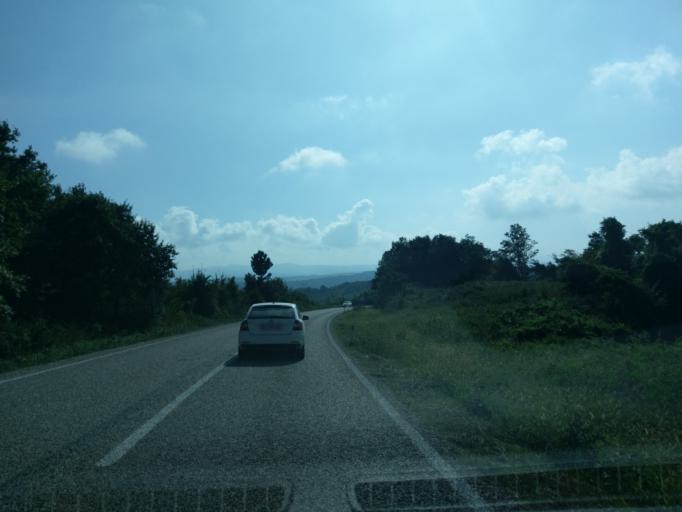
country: TR
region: Sinop
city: Erfelek
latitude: 41.9690
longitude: 34.8620
